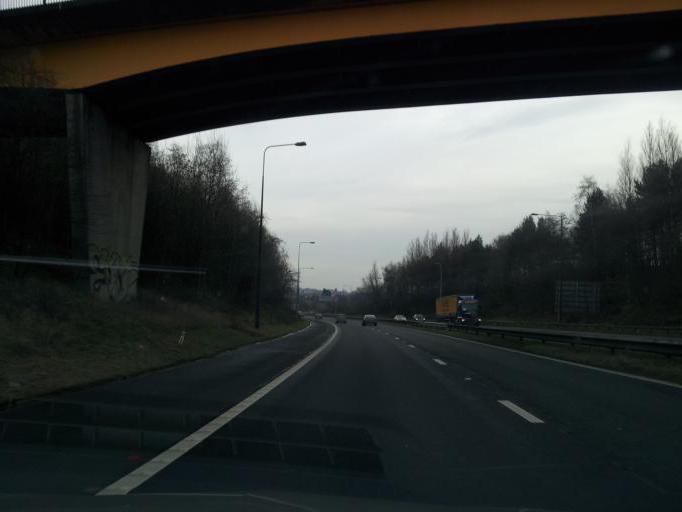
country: GB
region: England
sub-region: Borough of Oldham
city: Royton
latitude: 53.5636
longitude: -2.1534
